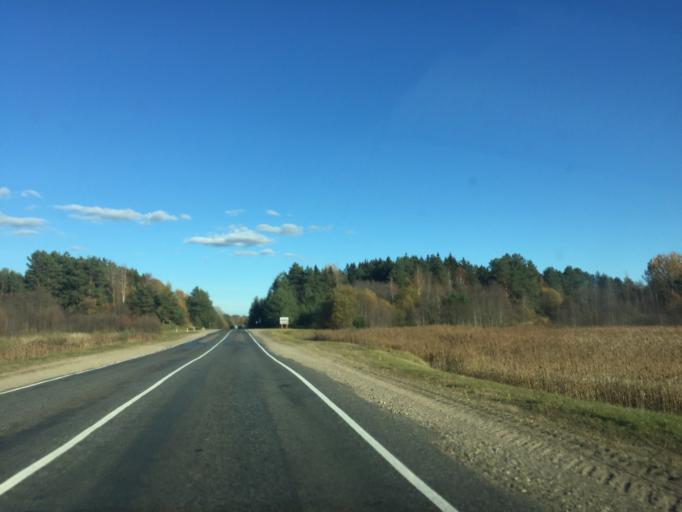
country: BY
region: Vitebsk
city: Dzisna
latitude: 55.2461
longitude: 28.0872
